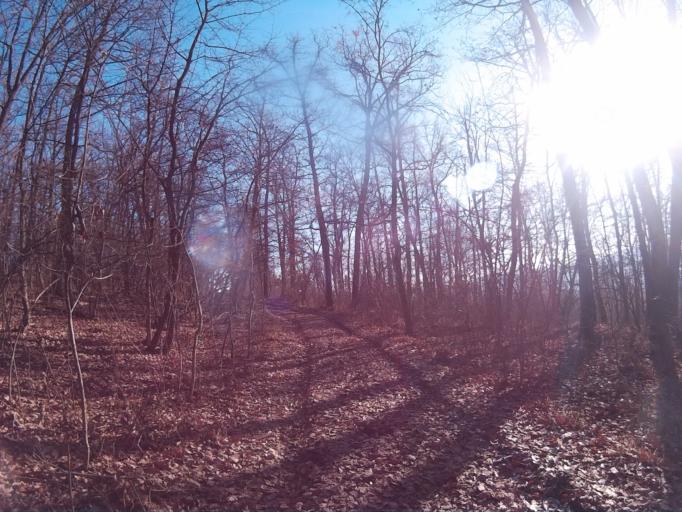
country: HU
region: Borsod-Abauj-Zemplen
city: Rudabanya
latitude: 48.4884
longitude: 20.5776
